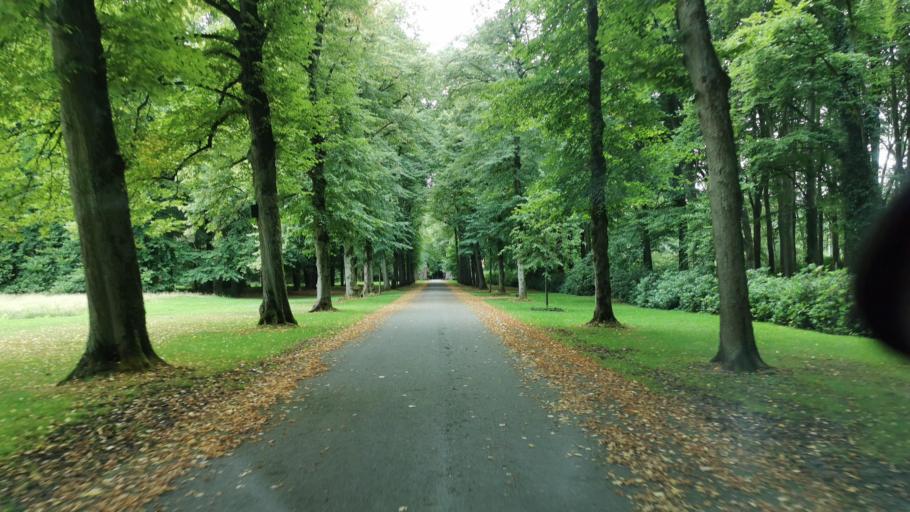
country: NL
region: Overijssel
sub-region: Gemeente Enschede
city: Enschede
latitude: 52.2341
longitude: 6.9421
